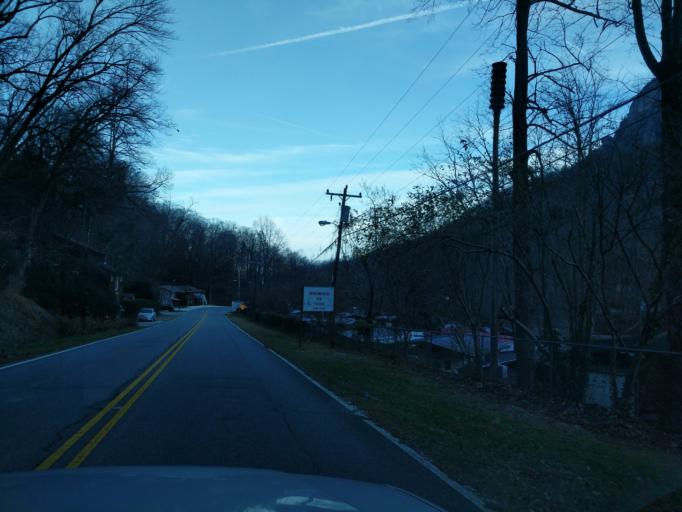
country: US
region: North Carolina
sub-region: Rutherford County
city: Lake Lure
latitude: 35.4419
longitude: -82.2582
